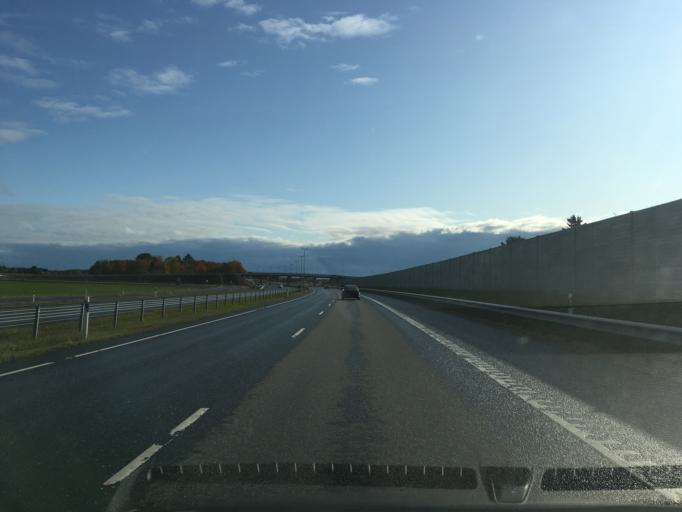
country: EE
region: Harju
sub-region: Rae vald
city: Vaida
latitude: 59.1836
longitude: 25.0767
